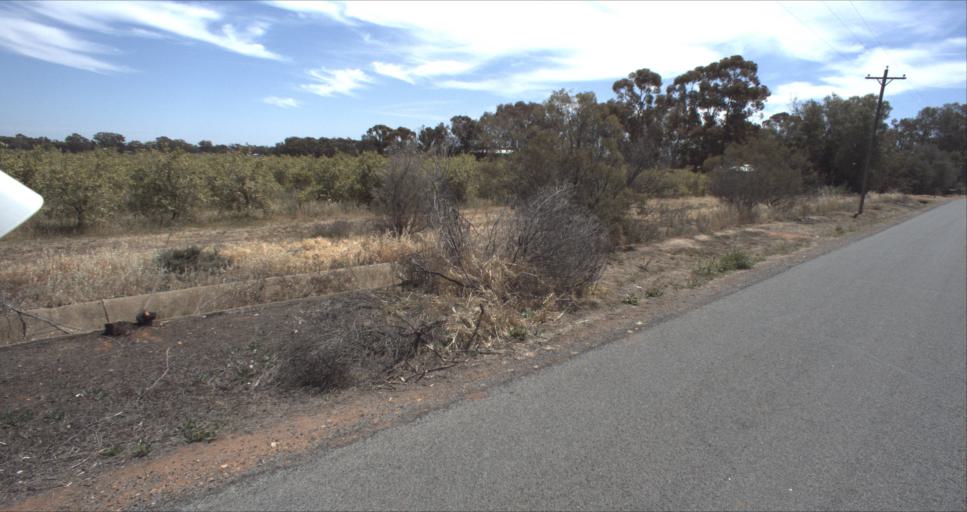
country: AU
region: New South Wales
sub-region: Leeton
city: Leeton
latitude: -34.5827
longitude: 146.4271
